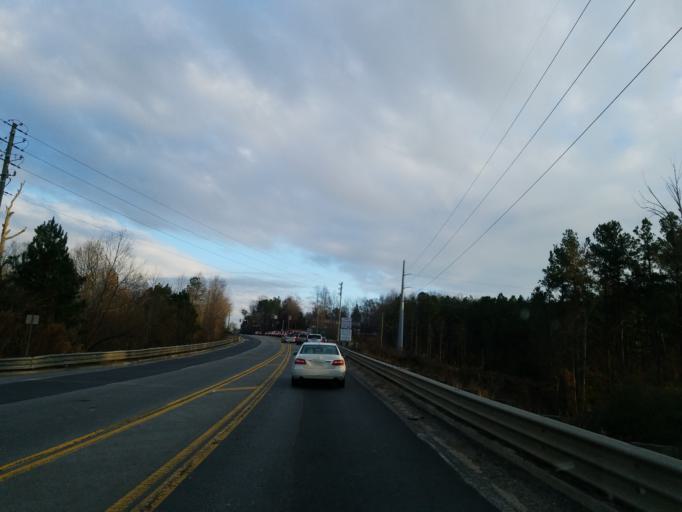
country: US
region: Georgia
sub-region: Forsyth County
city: Cumming
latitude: 34.2644
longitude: -84.0892
